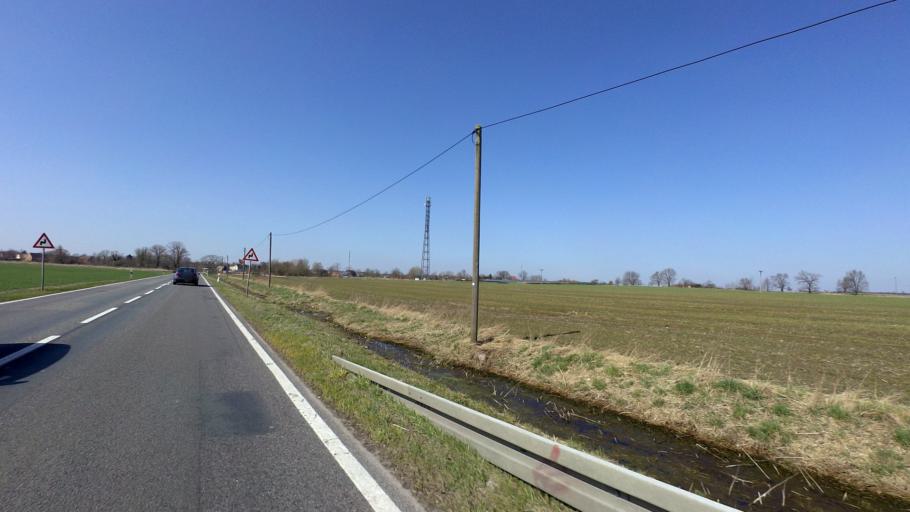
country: DE
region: Brandenburg
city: Ruthnick
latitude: 52.9014
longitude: 12.9824
